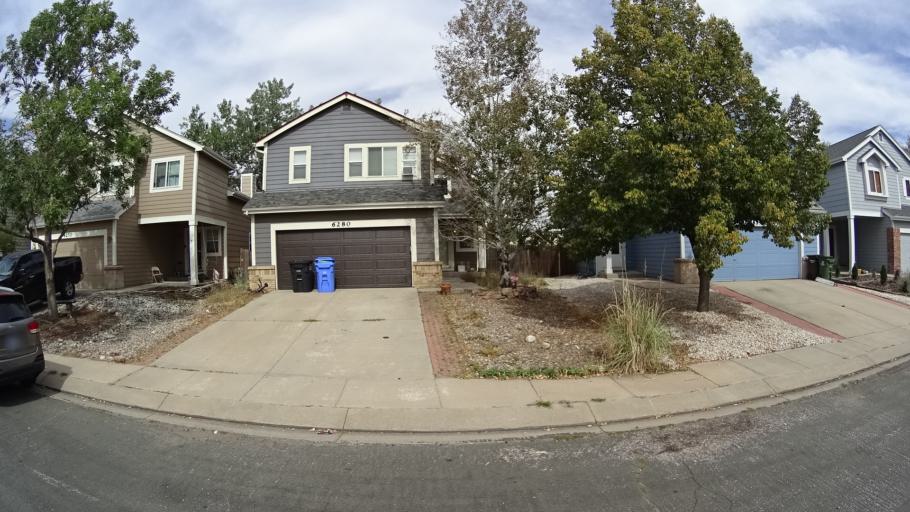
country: US
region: Colorado
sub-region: El Paso County
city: Cimarron Hills
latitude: 38.9054
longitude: -104.7035
